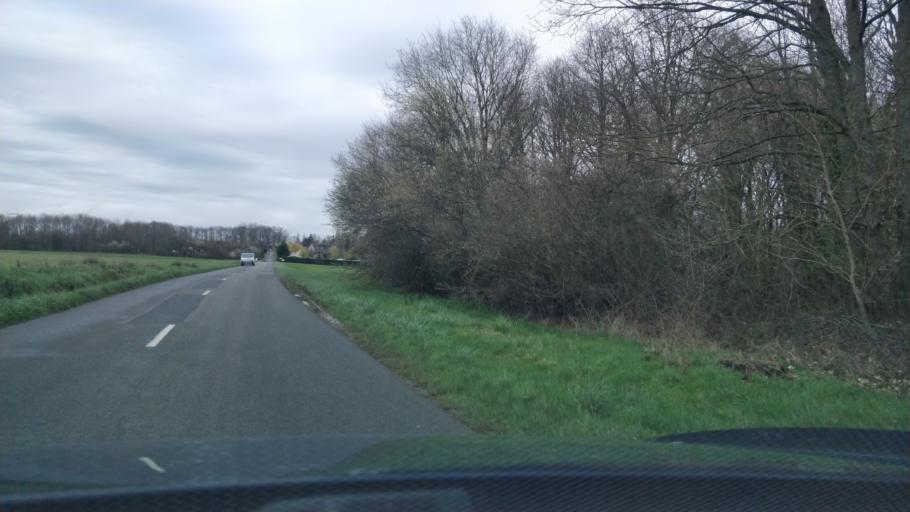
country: FR
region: Ile-de-France
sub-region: Departement de l'Essonne
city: Saint-Maurice-Montcouronne
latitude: 48.5860
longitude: 2.1068
